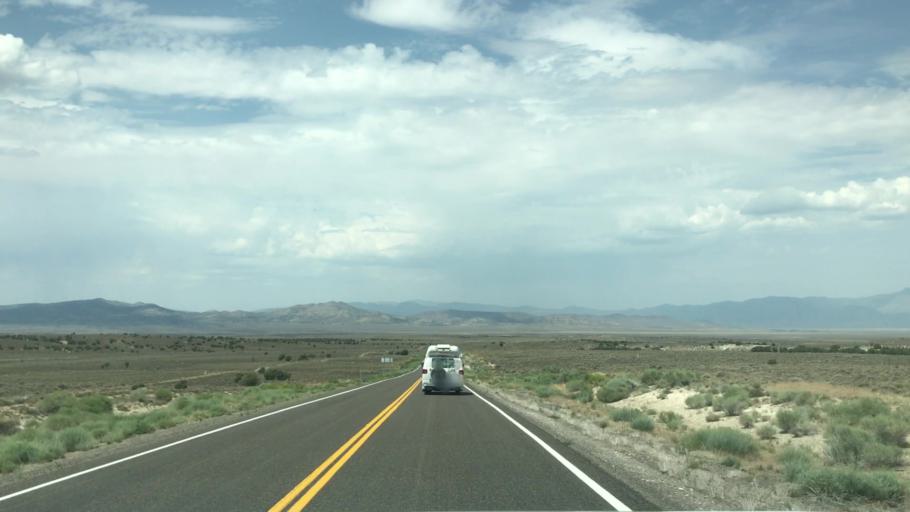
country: US
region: Nevada
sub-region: Eureka County
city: Eureka
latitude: 39.3944
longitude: -115.5267
